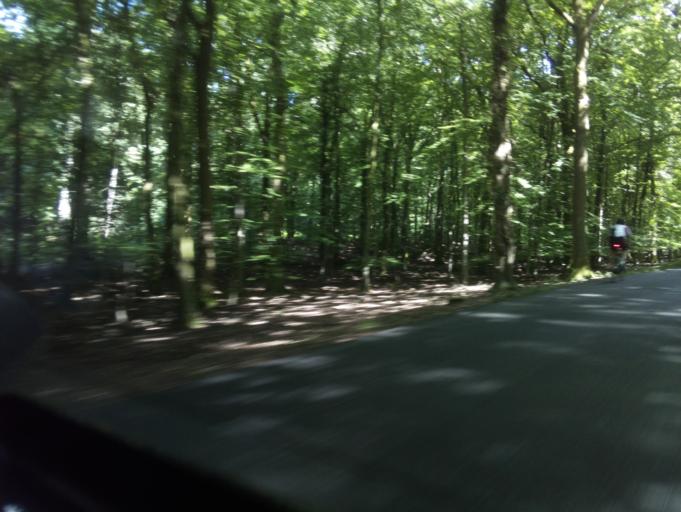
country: GB
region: England
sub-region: Gloucestershire
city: Cinderford
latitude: 51.7842
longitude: -2.4984
